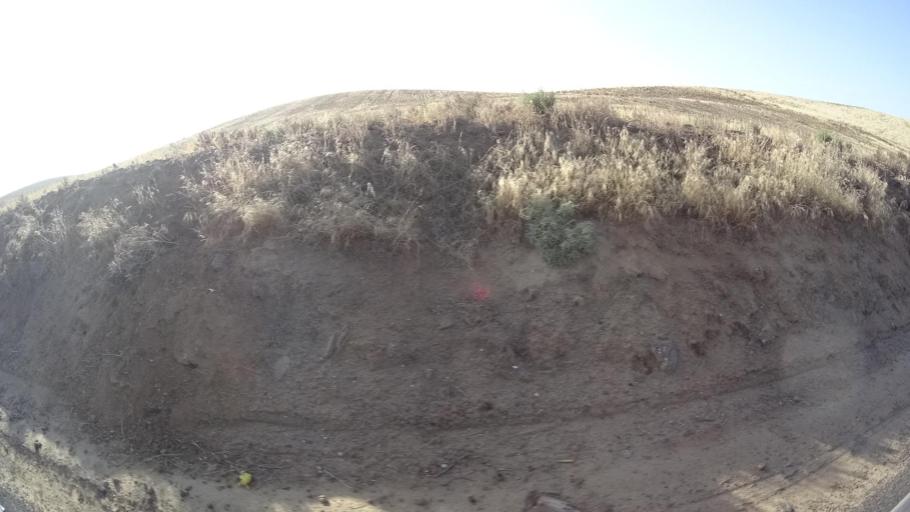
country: US
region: California
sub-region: Tulare County
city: Richgrove
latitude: 35.6592
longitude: -119.0794
